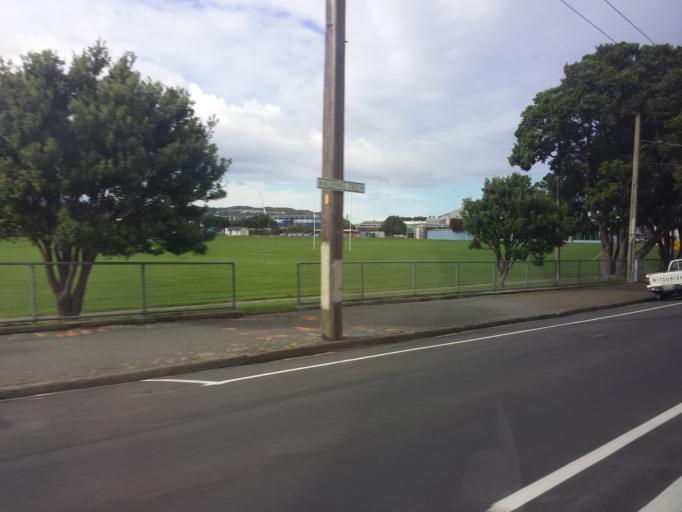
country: NZ
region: Wellington
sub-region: Wellington City
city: Wellington
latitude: -41.3129
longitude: 174.7931
